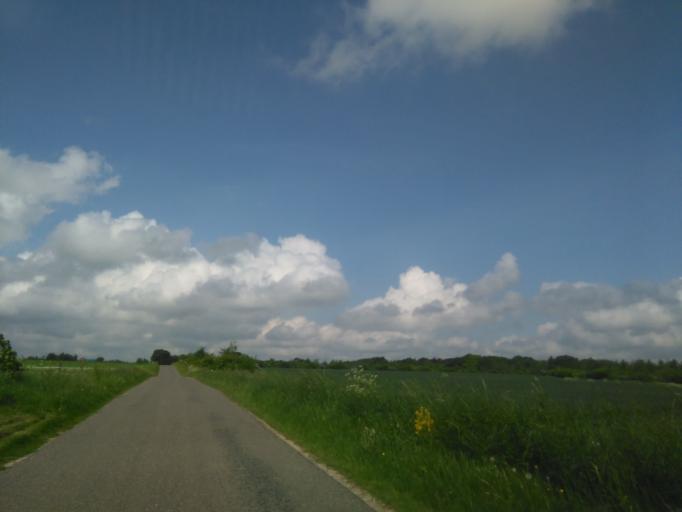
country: DK
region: Central Jutland
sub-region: Skanderborg Kommune
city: Skovby
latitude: 56.2051
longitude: 9.9516
